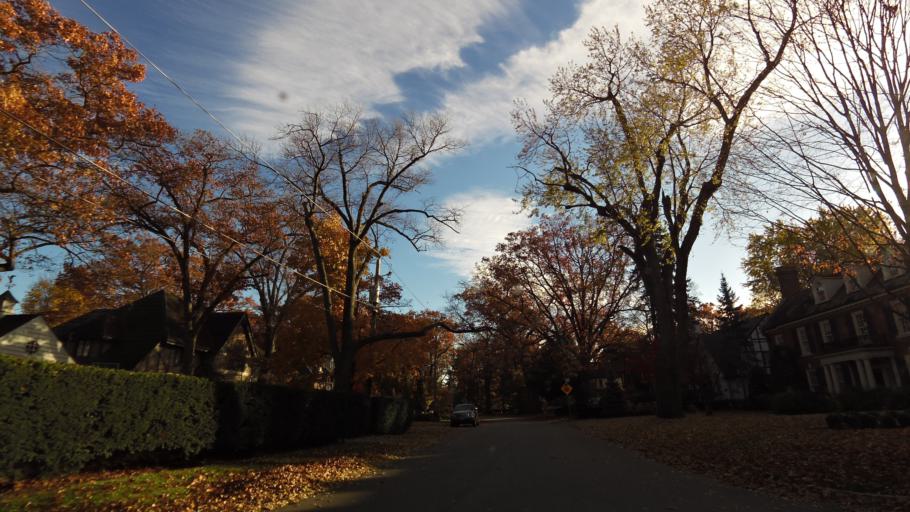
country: CA
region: Ontario
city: Etobicoke
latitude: 43.6538
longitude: -79.5049
